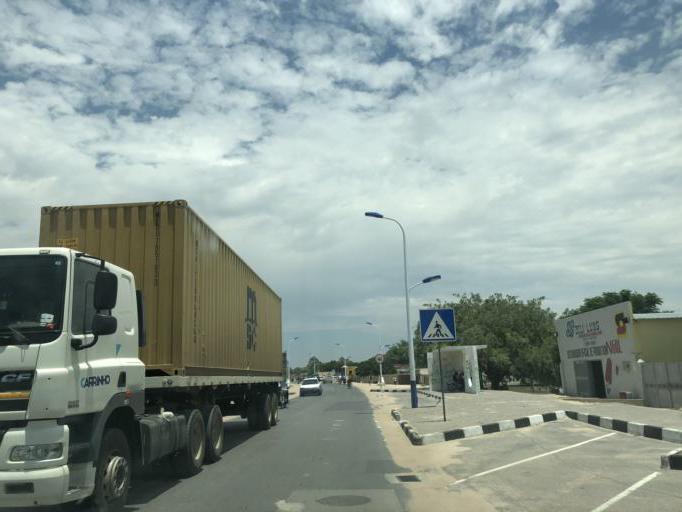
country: AO
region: Cunene
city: Ondjiva
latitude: -17.0730
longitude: 15.7329
